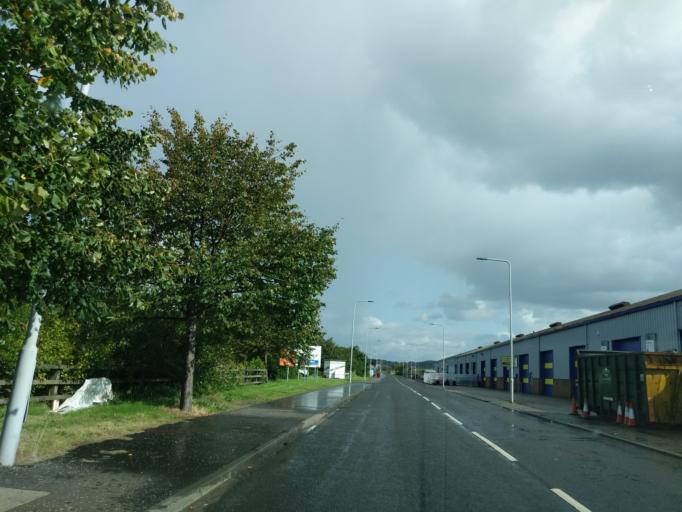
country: GB
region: Scotland
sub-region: Fife
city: Rosyth
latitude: 56.0255
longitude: -3.4363
